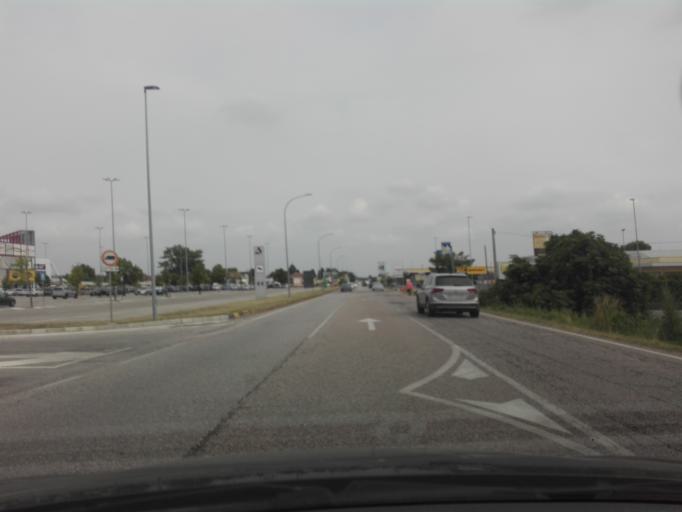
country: IT
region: Veneto
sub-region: Provincia di Rovigo
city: Rovigo
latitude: 45.0874
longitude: 11.7854
